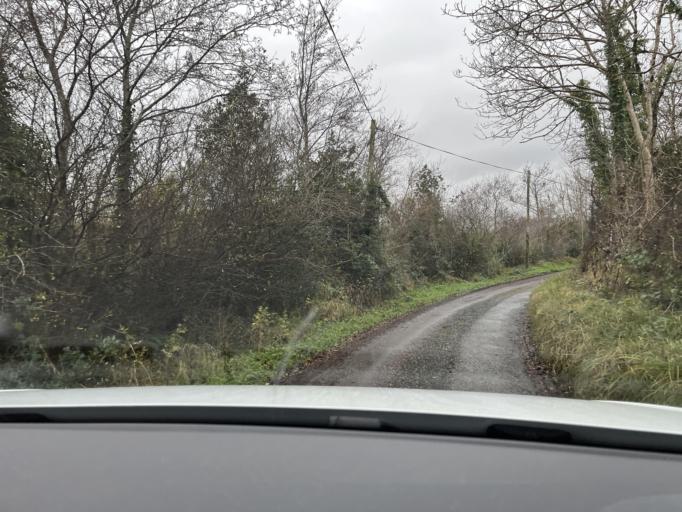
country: IE
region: Connaught
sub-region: County Leitrim
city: Manorhamilton
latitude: 54.2856
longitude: -8.1202
